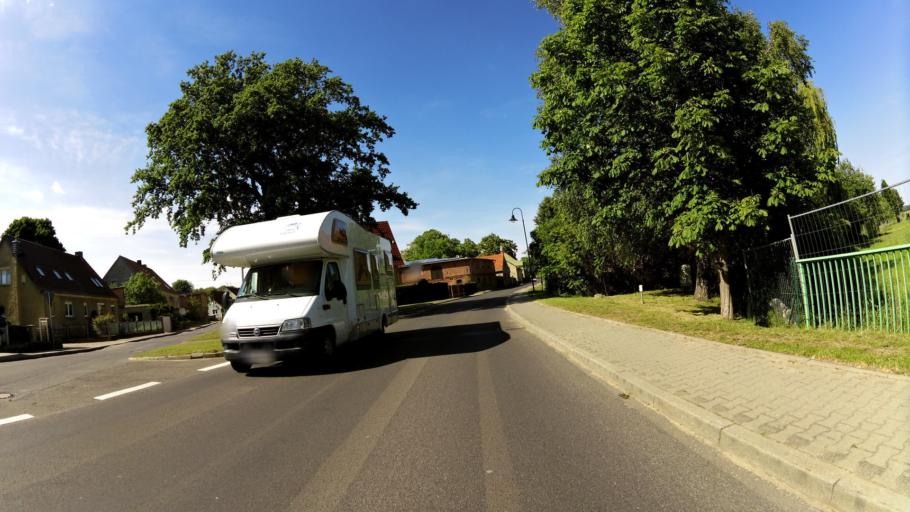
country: DE
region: Brandenburg
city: Jacobsdorf
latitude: 52.3363
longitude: 14.3537
